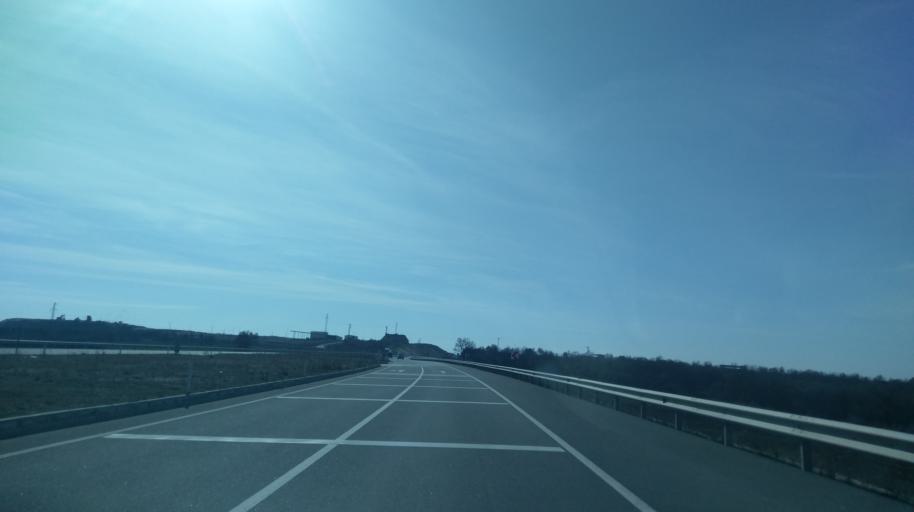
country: TR
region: Edirne
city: Kesan
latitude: 40.9290
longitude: 26.6362
